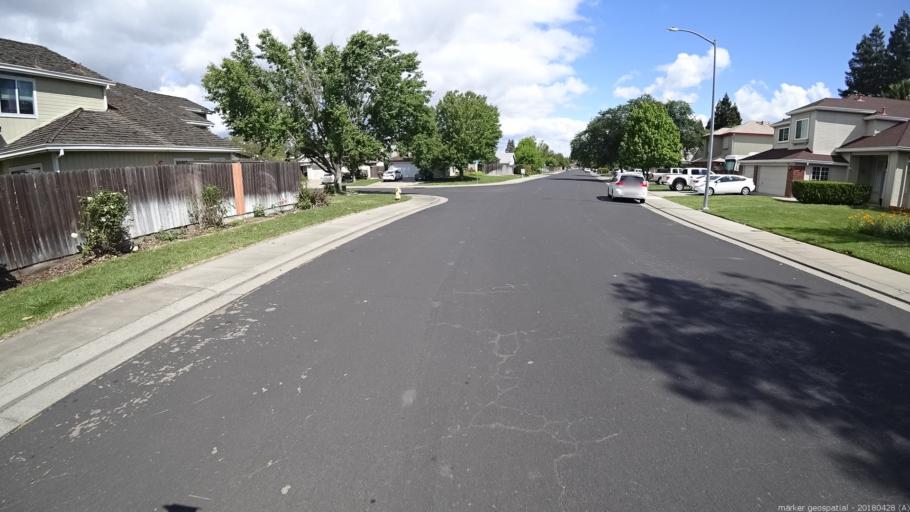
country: US
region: California
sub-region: Yolo County
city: West Sacramento
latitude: 38.5429
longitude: -121.5546
